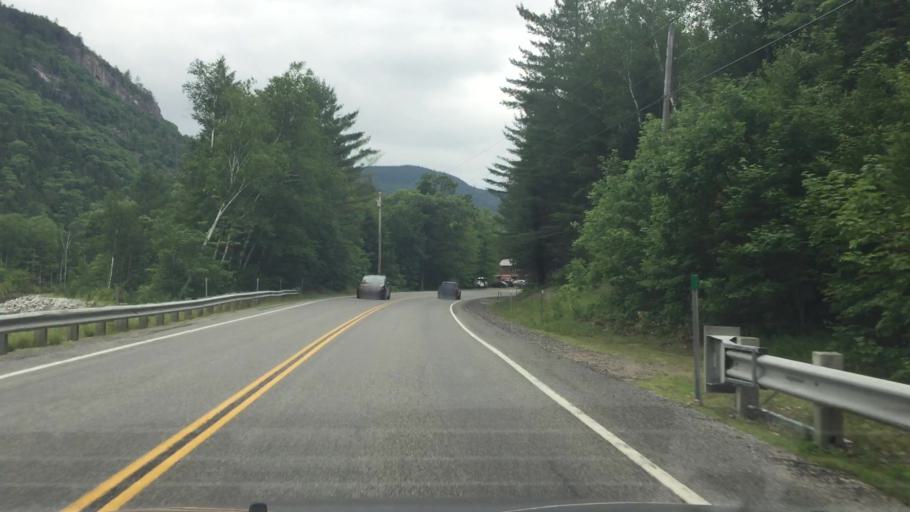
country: US
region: New Hampshire
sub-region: Carroll County
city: North Conway
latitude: 44.1361
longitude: -71.3607
